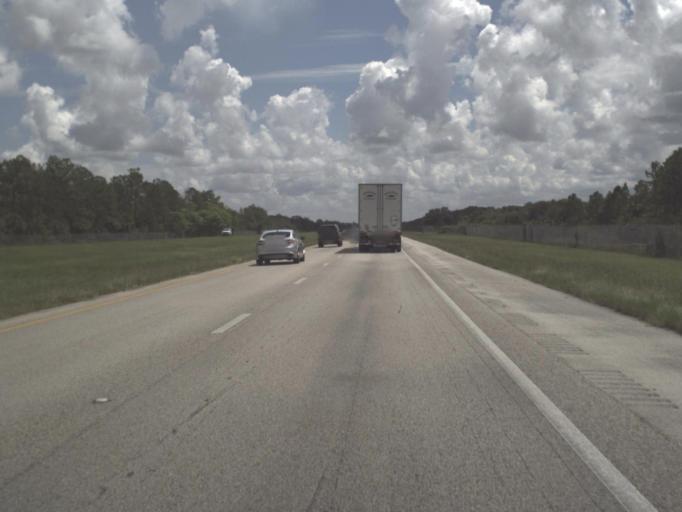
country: US
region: Florida
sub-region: Collier County
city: Orangetree
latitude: 26.1529
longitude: -81.5214
